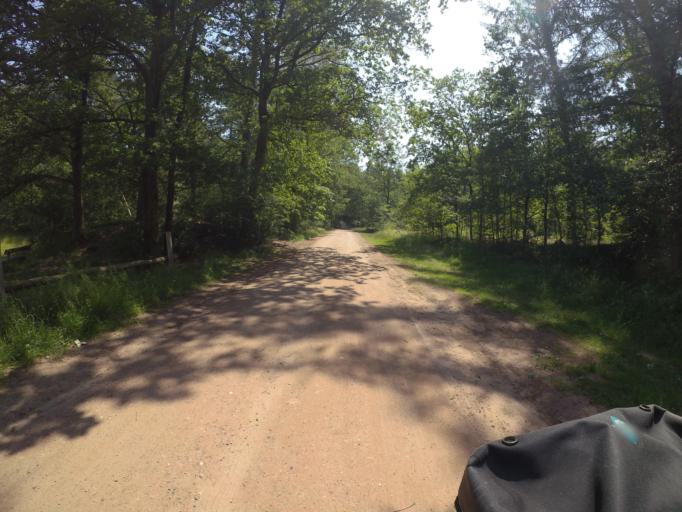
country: NL
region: Drenthe
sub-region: Gemeente De Wolden
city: Ruinen
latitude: 52.7289
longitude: 6.3805
